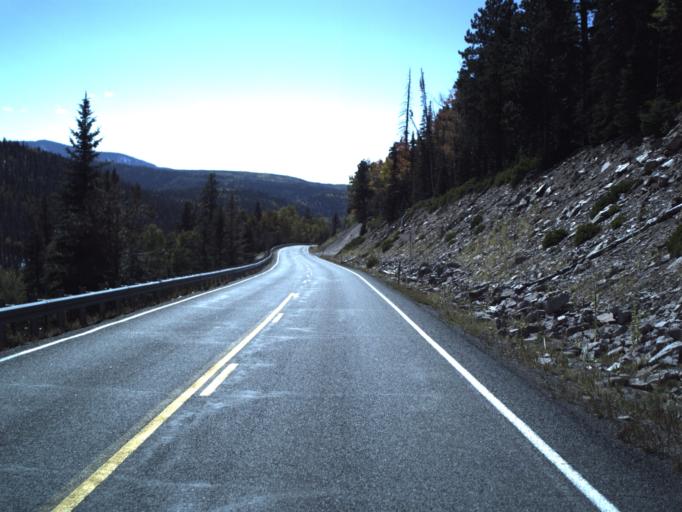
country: US
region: Utah
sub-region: Piute County
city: Junction
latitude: 38.3180
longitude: -112.3890
